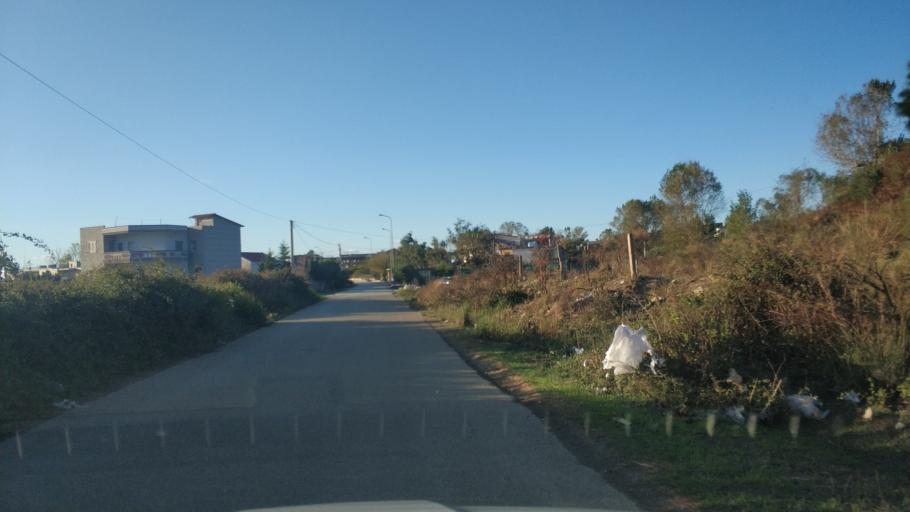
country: AL
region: Vlore
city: Vlore
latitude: 40.5051
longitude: 19.4148
